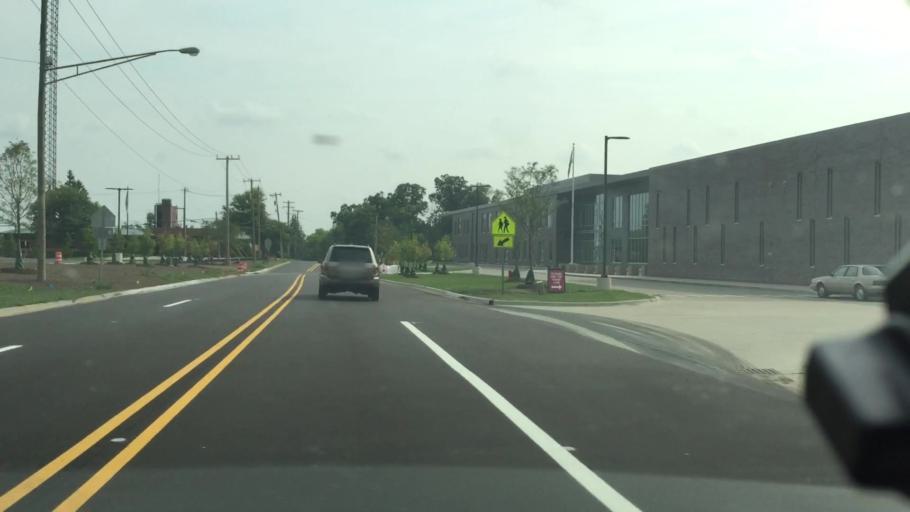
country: US
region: Michigan
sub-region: Oakland County
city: Bloomfield Hills
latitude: 42.5796
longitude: -83.2847
